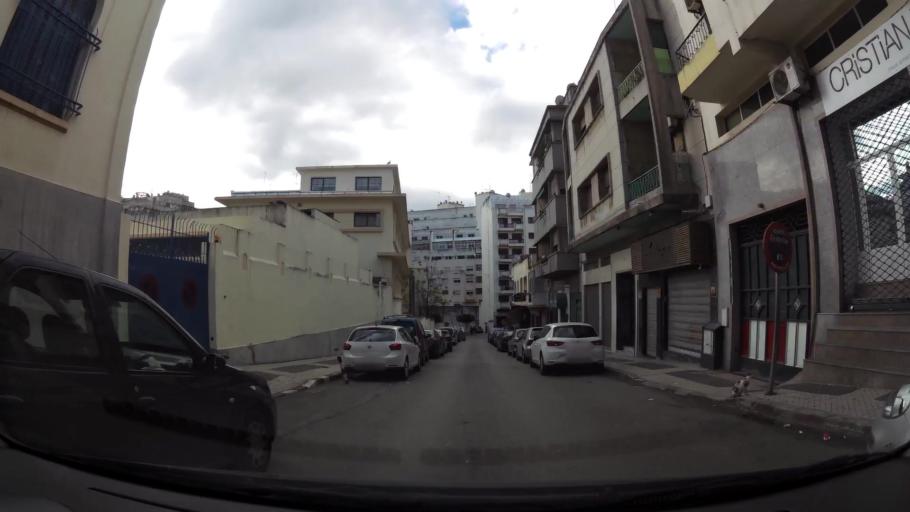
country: MA
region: Tanger-Tetouan
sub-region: Tanger-Assilah
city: Tangier
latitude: 35.7776
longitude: -5.8092
